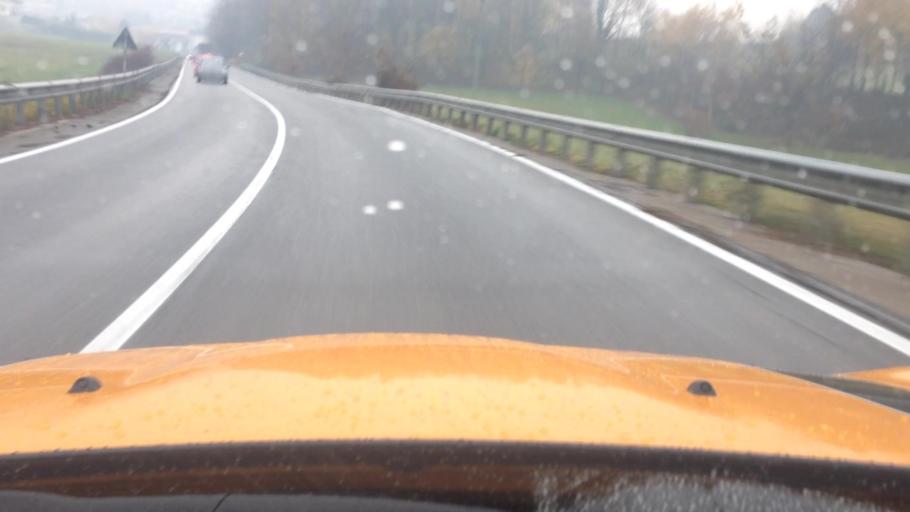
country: IT
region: Lombardy
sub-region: Provincia di Como
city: Senna Comasco
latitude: 45.7549
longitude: 9.1198
